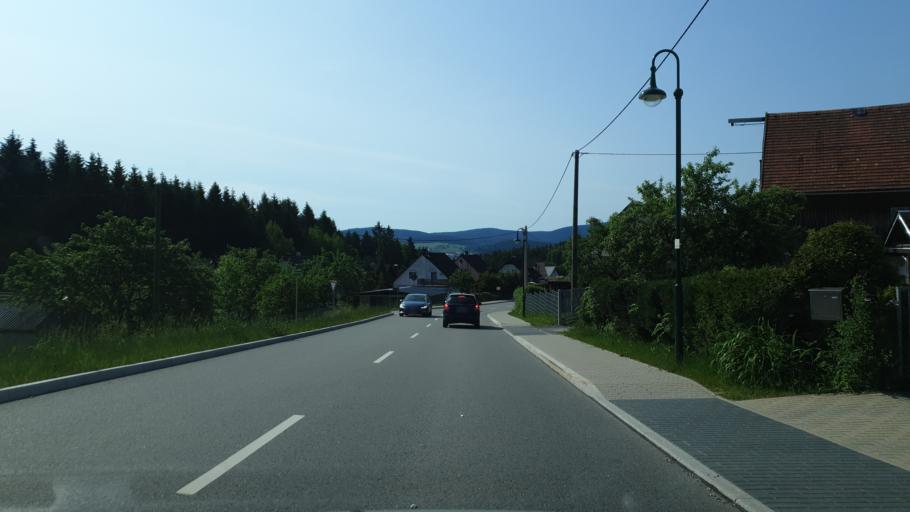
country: DE
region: Saxony
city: Zschorlau
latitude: 50.5338
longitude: 12.6209
